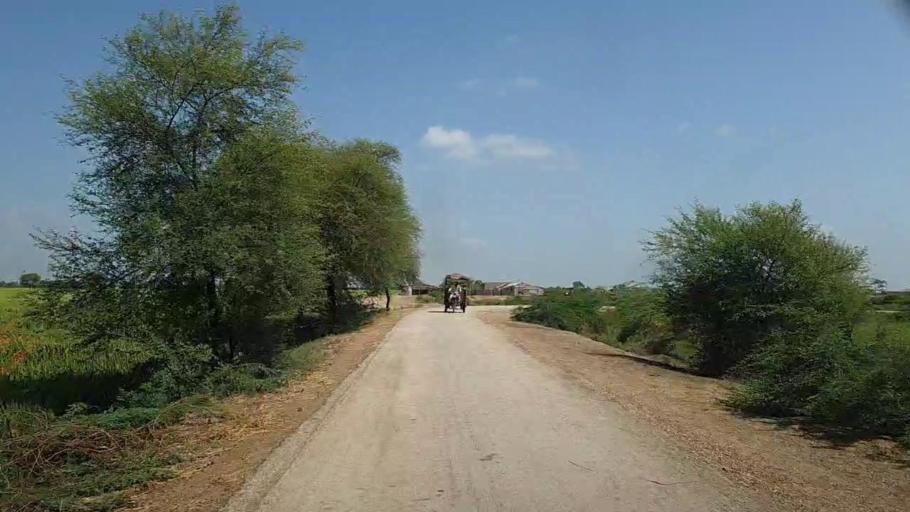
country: PK
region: Sindh
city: Kario
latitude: 24.6433
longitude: 68.5673
